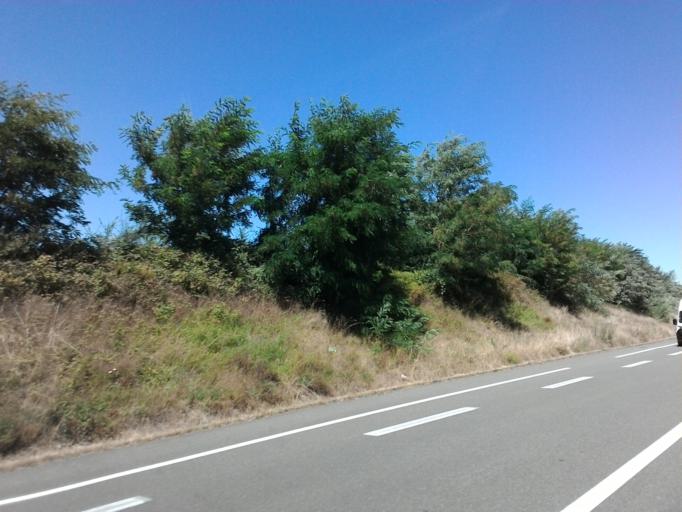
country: FR
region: Franche-Comte
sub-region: Departement du Jura
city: Montmorot
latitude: 46.6708
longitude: 5.5094
